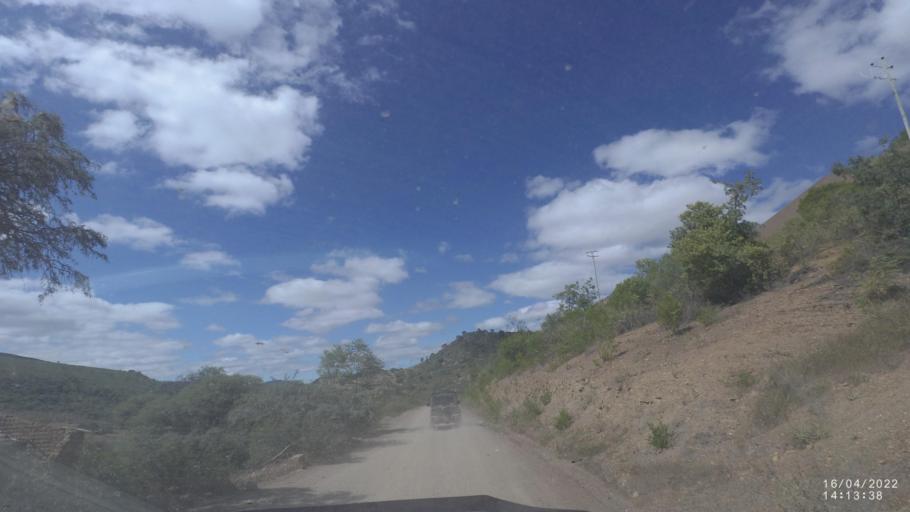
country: BO
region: Cochabamba
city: Mizque
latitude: -18.0582
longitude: -65.5093
